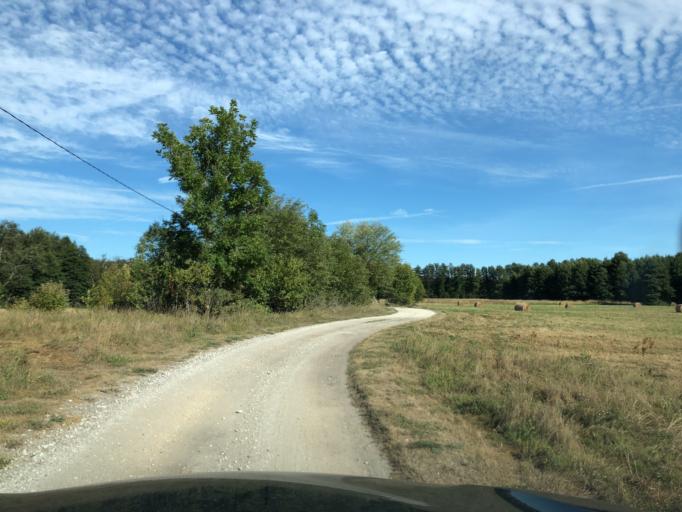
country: EE
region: Laeaene
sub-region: Haapsalu linn
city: Haapsalu
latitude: 58.7821
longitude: 23.4783
